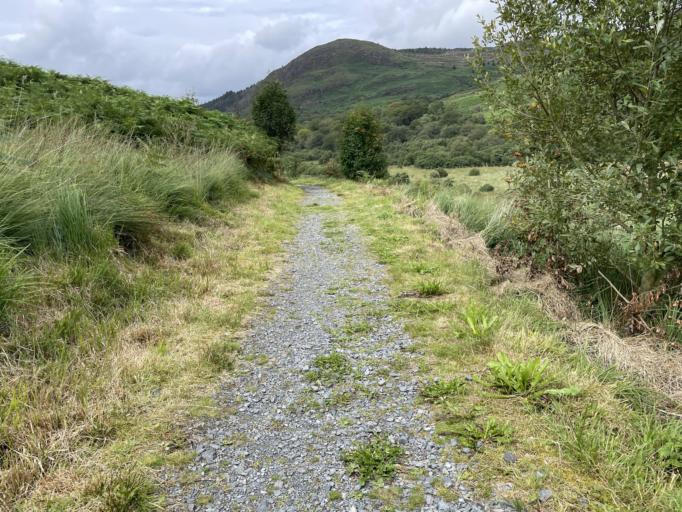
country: GB
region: Scotland
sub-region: Dumfries and Galloway
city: Newton Stewart
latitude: 55.0903
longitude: -4.4679
